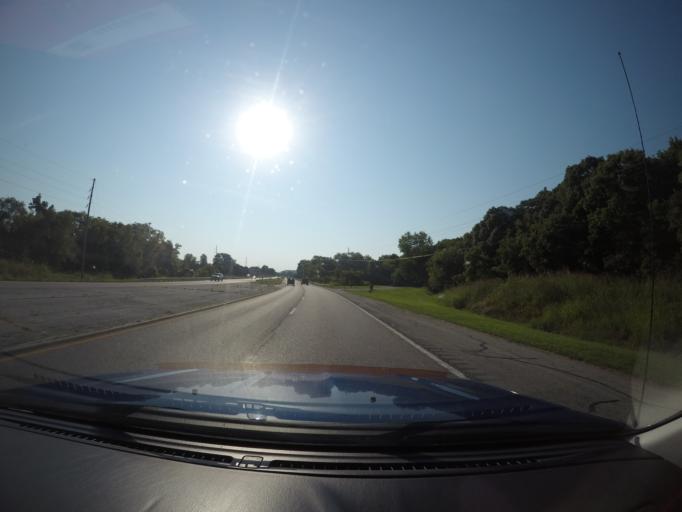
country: US
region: Kansas
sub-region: Wyandotte County
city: Edwardsville
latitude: 39.0637
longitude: -94.8315
